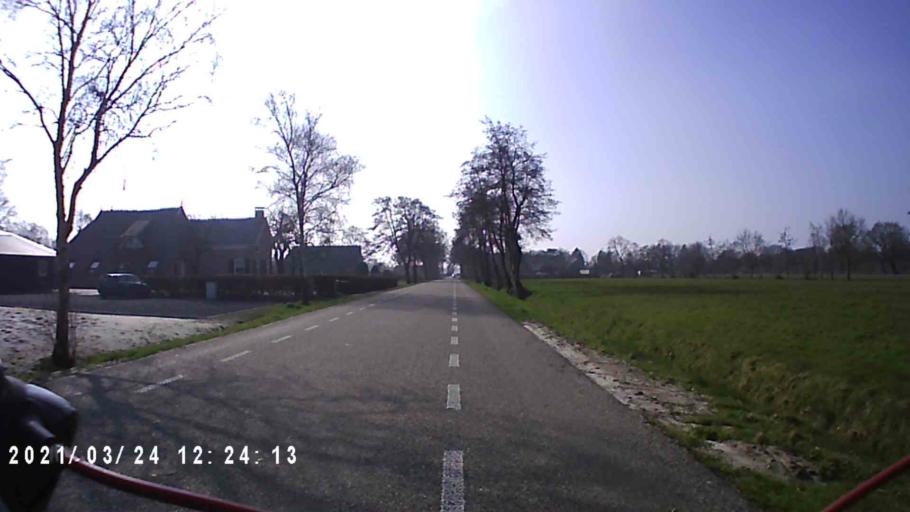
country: NL
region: Groningen
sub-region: Gemeente Leek
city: Leek
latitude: 53.1839
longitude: 6.3929
